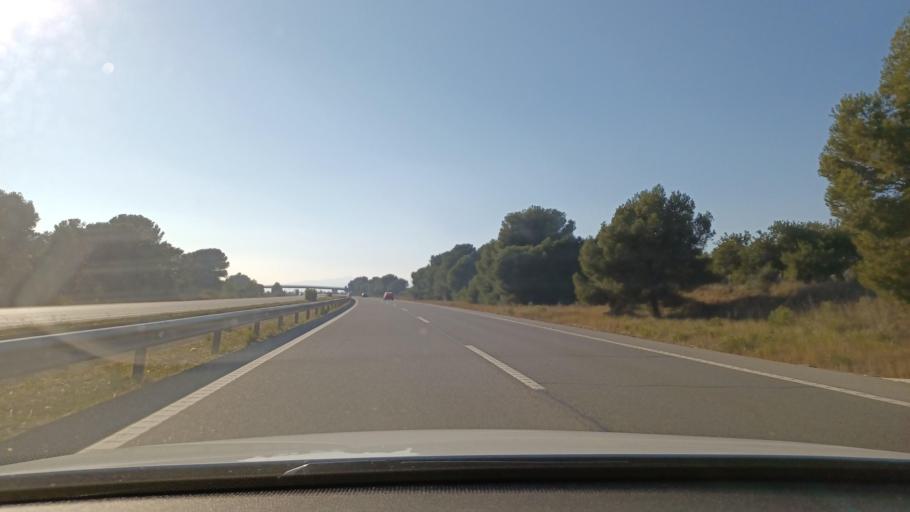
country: ES
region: Catalonia
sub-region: Provincia de Tarragona
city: Salou
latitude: 41.0987
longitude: 1.1005
